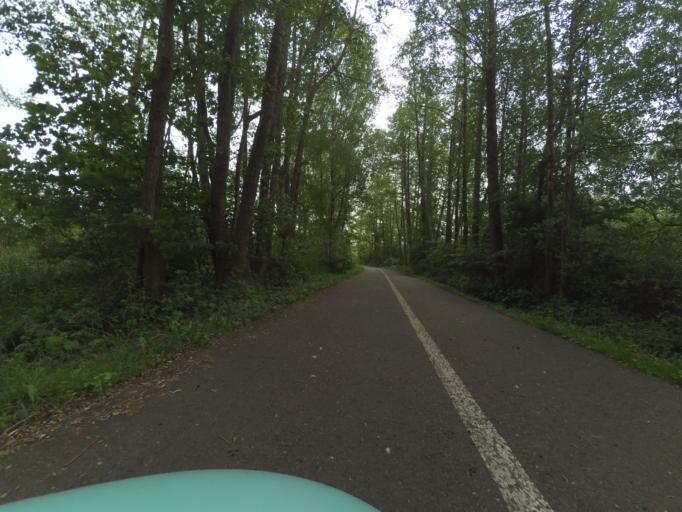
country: DE
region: Lower Saxony
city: Hagenburg
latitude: 52.4465
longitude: 9.3189
